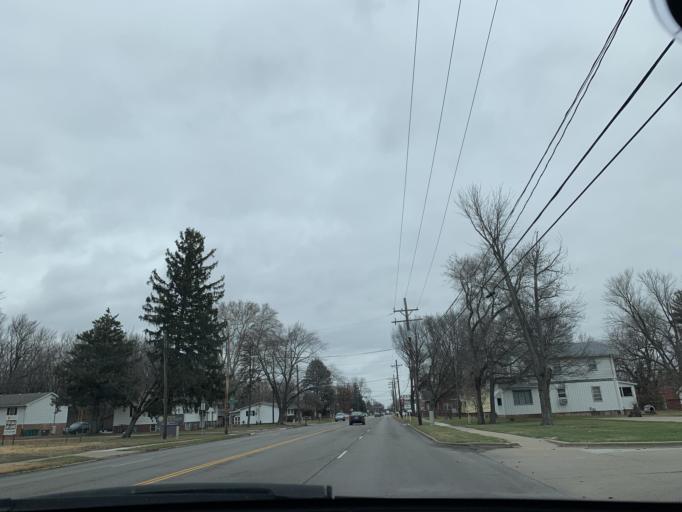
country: US
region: Illinois
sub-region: Sangamon County
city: Leland Grove
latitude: 39.8045
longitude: -89.6870
